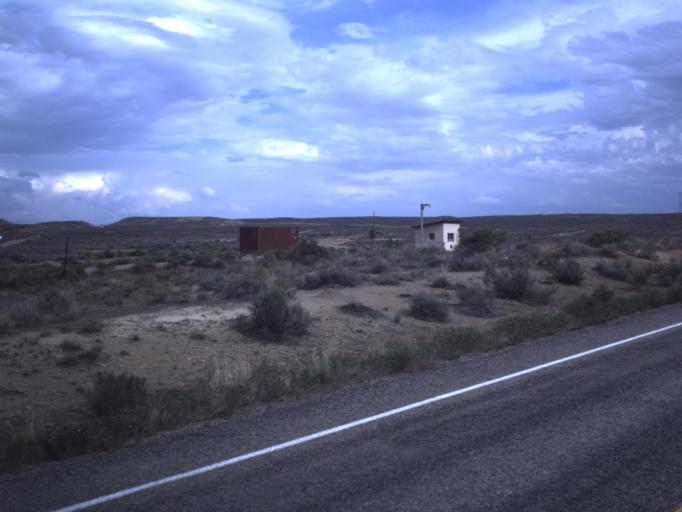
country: US
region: Colorado
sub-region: Rio Blanco County
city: Rangely
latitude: 40.0153
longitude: -109.1713
